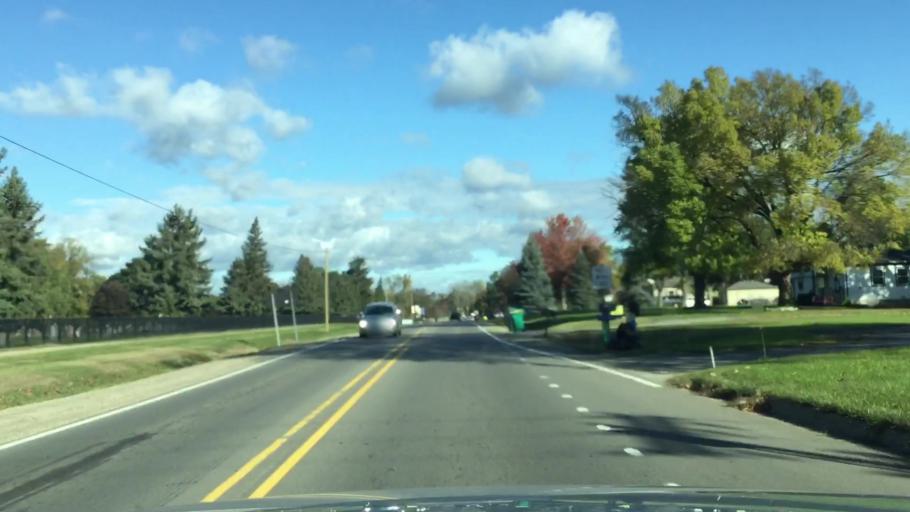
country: US
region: Michigan
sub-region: Oakland County
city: Waterford
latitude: 42.6680
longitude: -83.3866
